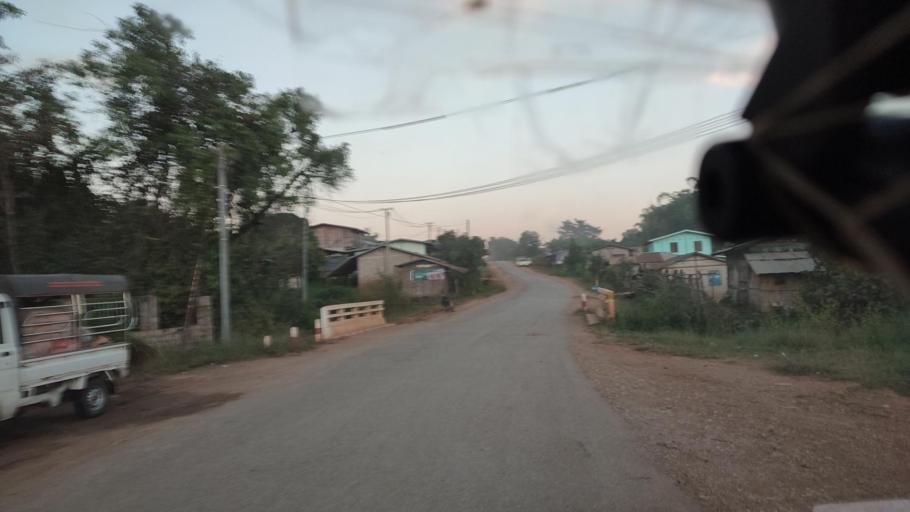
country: MM
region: Shan
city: Taunggyi
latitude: 21.0011
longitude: 97.9527
